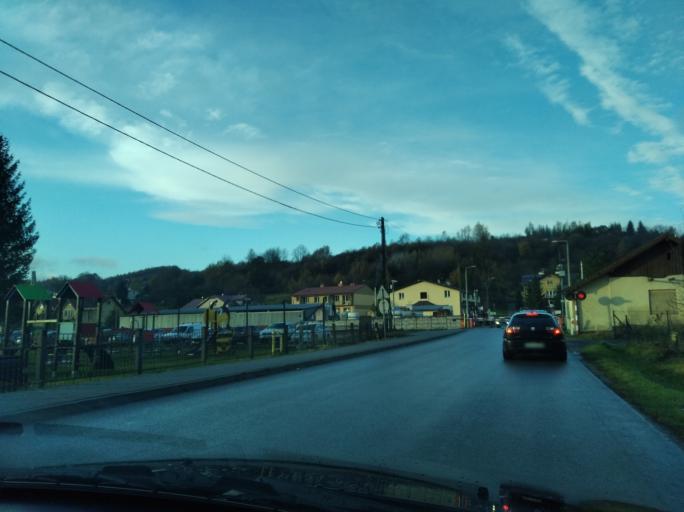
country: PL
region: Subcarpathian Voivodeship
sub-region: Powiat rzeszowski
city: Lubenia
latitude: 49.9338
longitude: 21.8991
